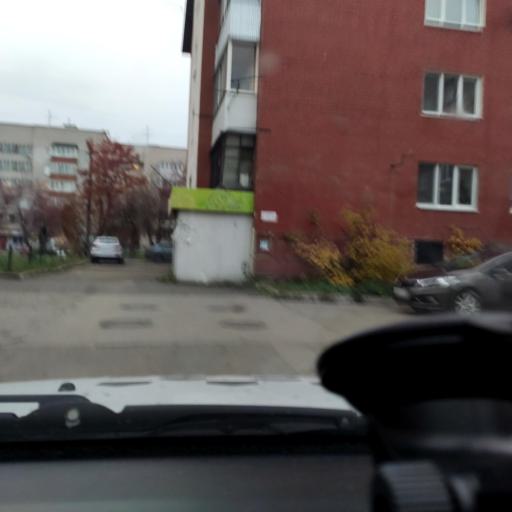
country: RU
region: Perm
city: Kondratovo
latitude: 57.9757
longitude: 56.1038
